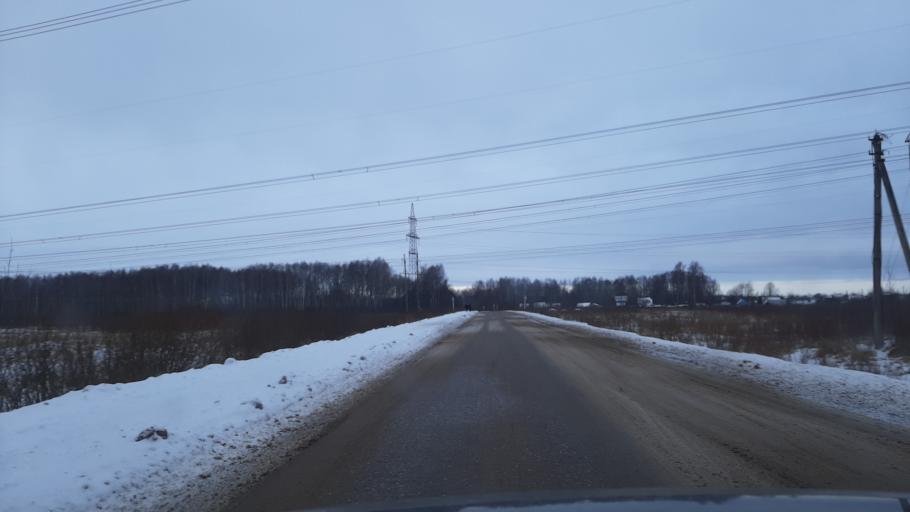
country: RU
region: Kostroma
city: Volgorechensk
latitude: 57.4441
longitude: 41.1413
